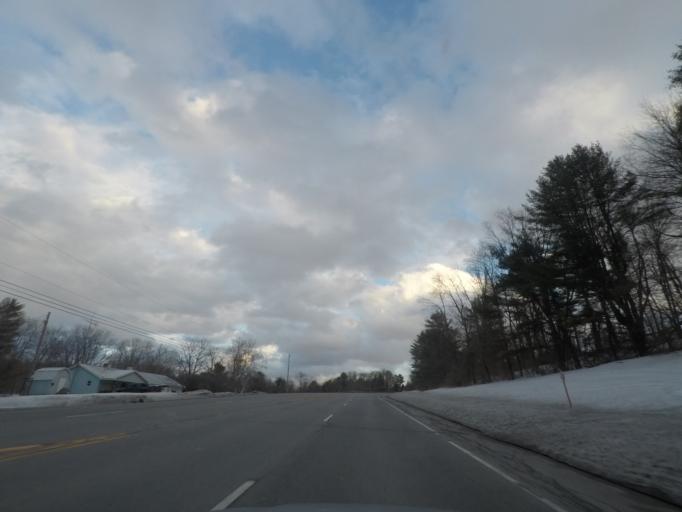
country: US
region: New York
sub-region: Herkimer County
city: Little Falls
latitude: 43.0243
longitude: -74.7868
